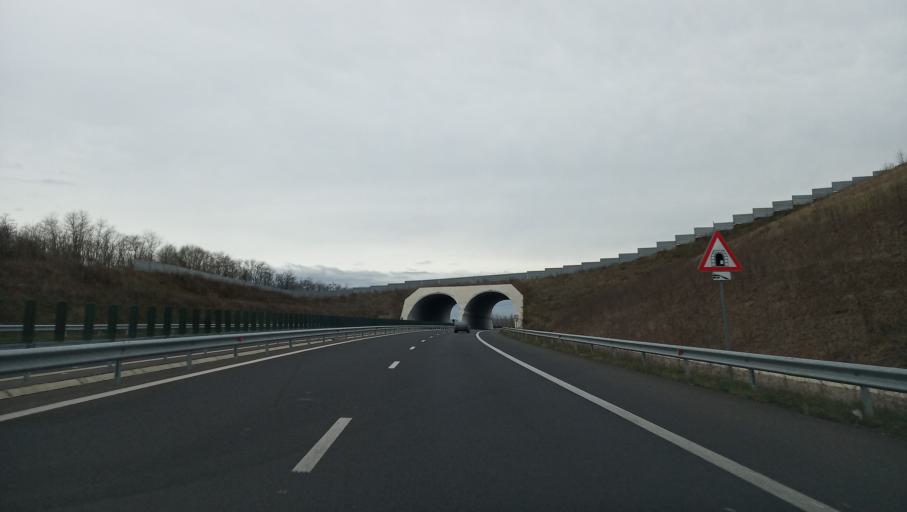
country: RO
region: Hunedoara
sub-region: Comuna Branisca
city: Branisca
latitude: 45.9380
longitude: 22.7411
